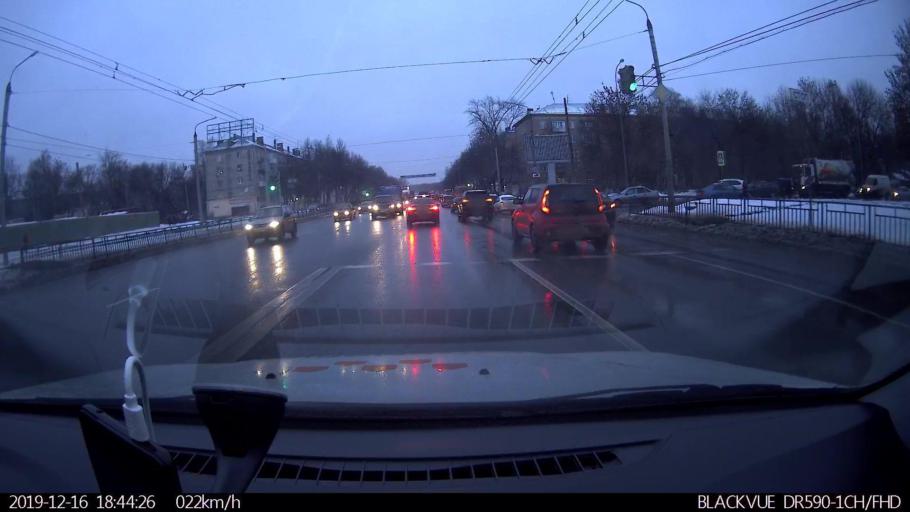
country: RU
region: Nizjnij Novgorod
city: Nizhniy Novgorod
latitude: 56.2623
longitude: 43.9084
